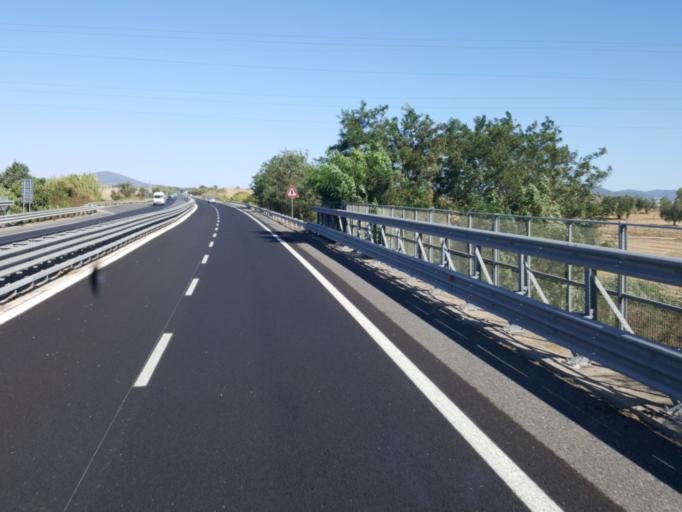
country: IT
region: Latium
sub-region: Provincia di Viterbo
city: Montalto di Castro
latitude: 42.3748
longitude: 11.5585
